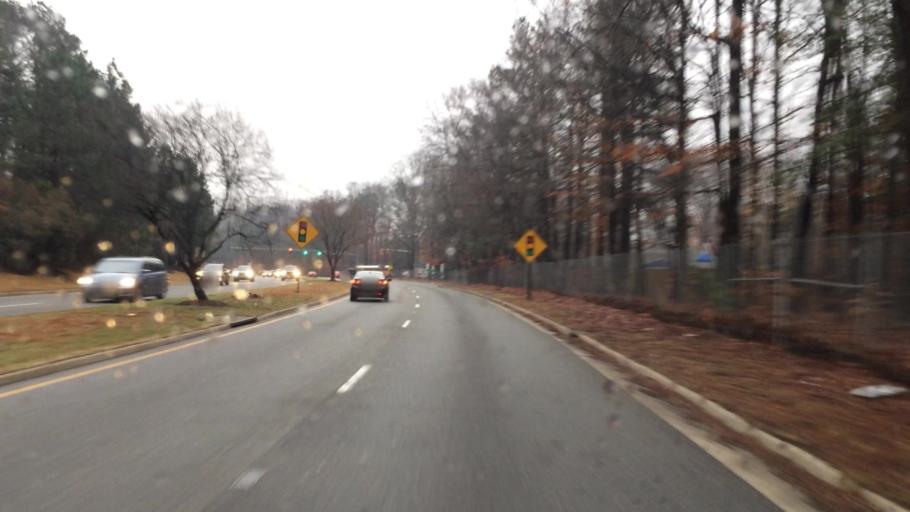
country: US
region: Virginia
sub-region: James City County
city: Williamsburg
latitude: 37.2516
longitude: -76.7296
